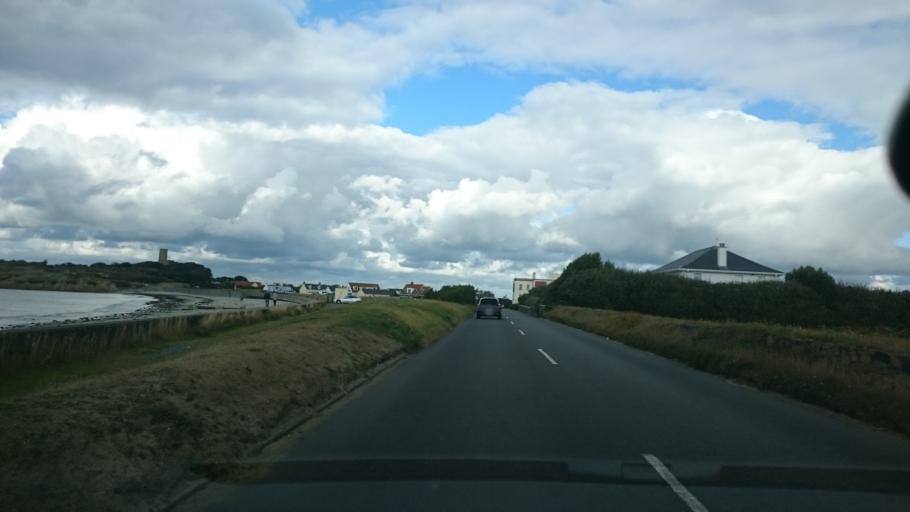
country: GG
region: St Peter Port
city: Saint Peter Port
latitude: 49.4515
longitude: -2.6500
